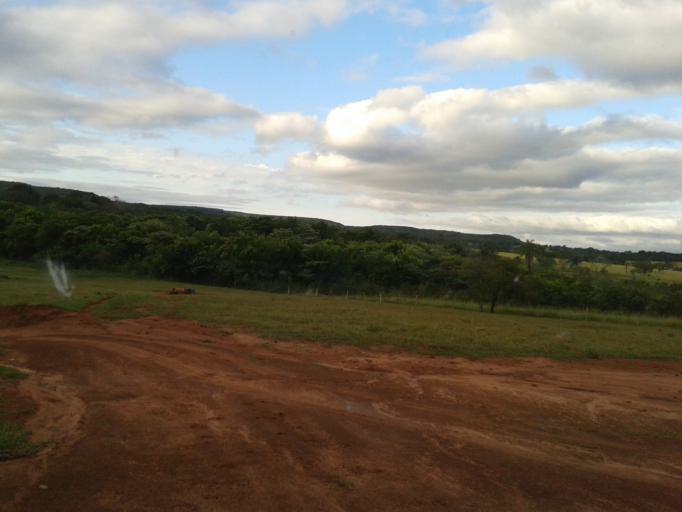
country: BR
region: Minas Gerais
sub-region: Campina Verde
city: Campina Verde
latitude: -19.4744
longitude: -49.6517
